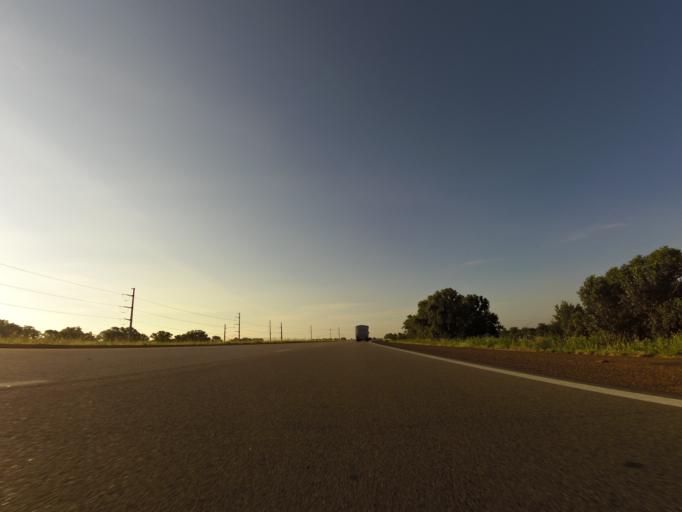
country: US
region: Kansas
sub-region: Sedgwick County
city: Maize
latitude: 37.7832
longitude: -97.4625
